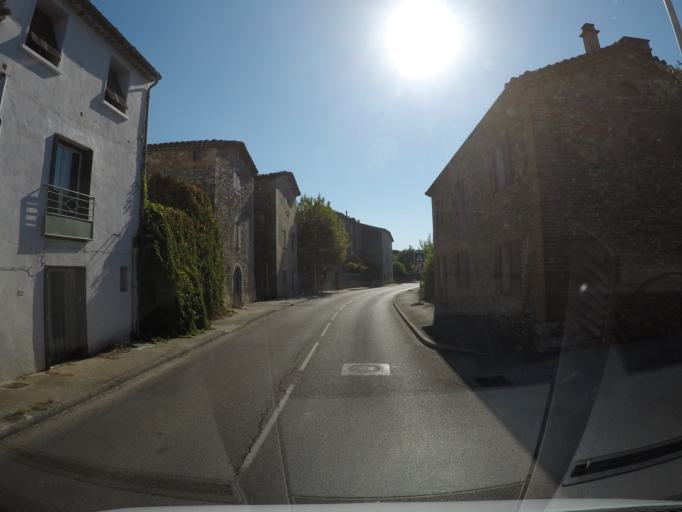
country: FR
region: Languedoc-Roussillon
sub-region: Departement du Gard
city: Boisset-et-Gaujac
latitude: 44.0268
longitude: 4.0218
